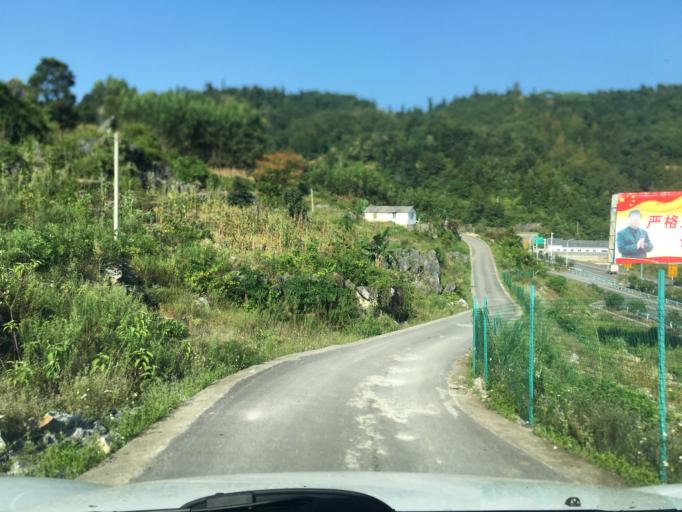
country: CN
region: Guangxi Zhuangzu Zizhiqu
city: Xinzhou
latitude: 25.4711
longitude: 105.7327
